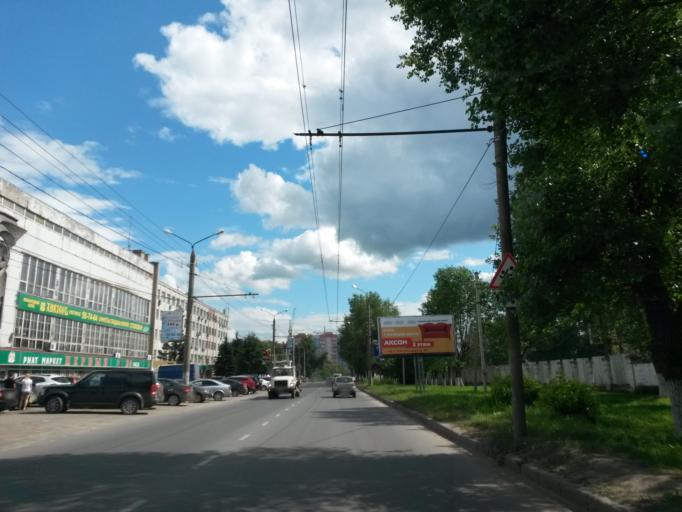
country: RU
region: Ivanovo
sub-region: Gorod Ivanovo
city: Ivanovo
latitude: 56.9964
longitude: 40.9603
